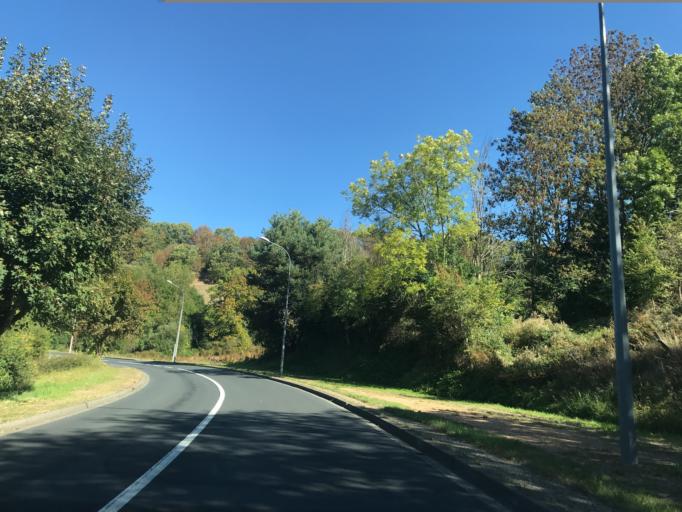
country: FR
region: Auvergne
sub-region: Departement du Puy-de-Dome
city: Gelles
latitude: 45.6895
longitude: 2.8083
